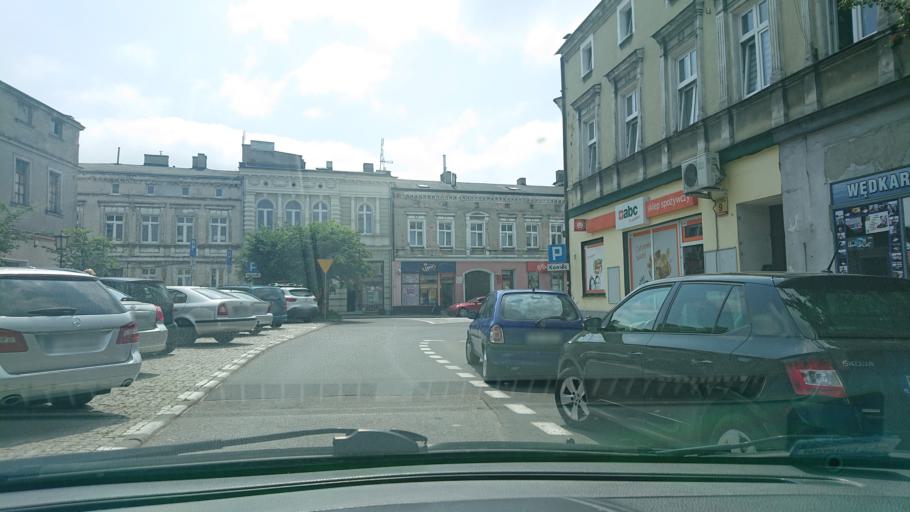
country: PL
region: Greater Poland Voivodeship
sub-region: Powiat gnieznienski
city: Gniezno
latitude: 52.5338
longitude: 17.5952
